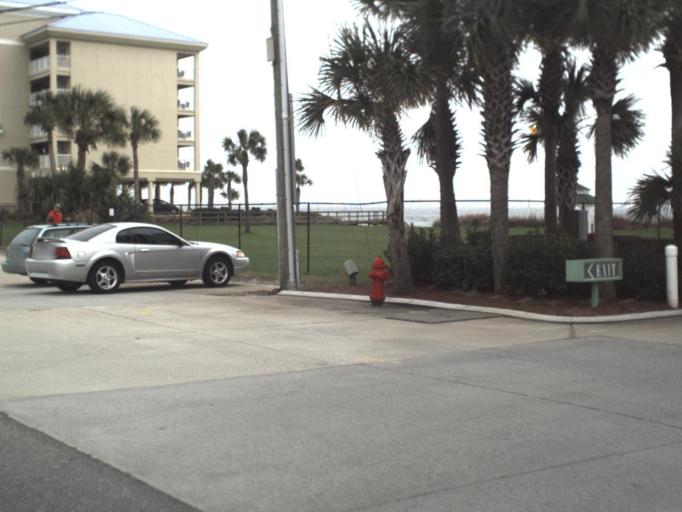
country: US
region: Florida
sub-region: Bay County
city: Laguna Beach
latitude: 30.2221
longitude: -85.8888
